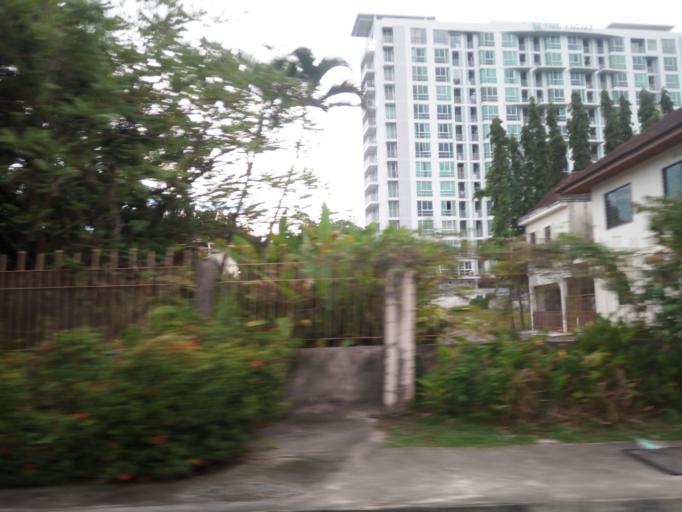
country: TH
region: Phuket
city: Ban Talat Nua
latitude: 7.8713
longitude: 98.3796
